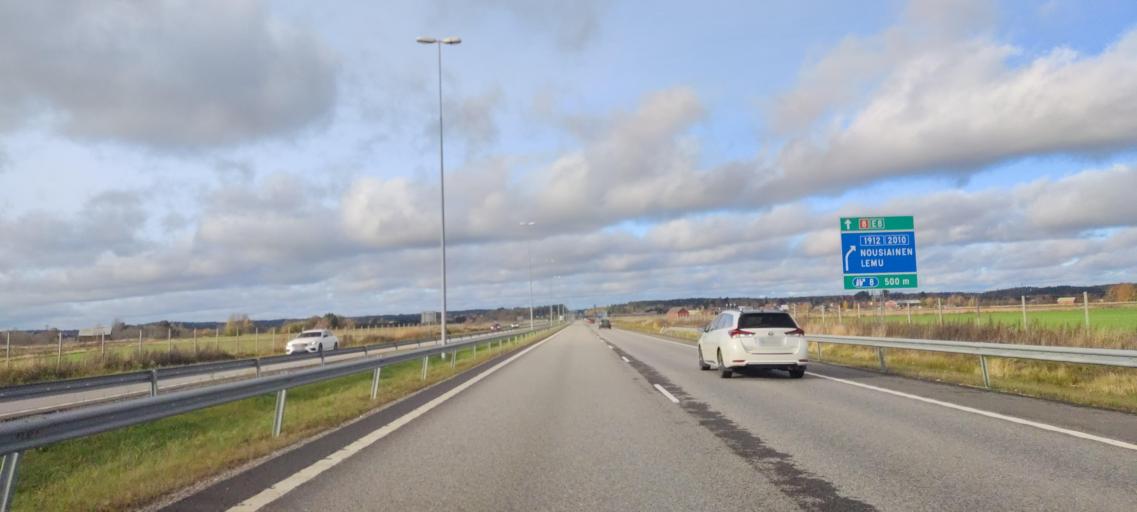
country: FI
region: Varsinais-Suomi
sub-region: Turku
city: Masku
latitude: 60.5852
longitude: 22.0877
